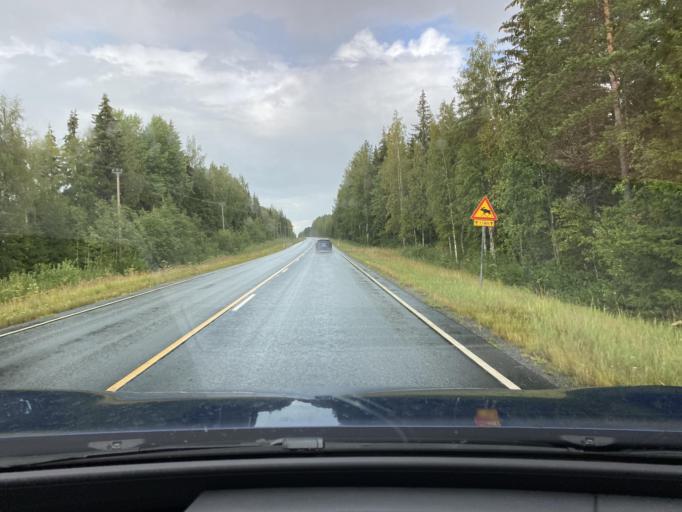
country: FI
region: Pirkanmaa
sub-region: Tampere
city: Haemeenkyroe
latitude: 61.5800
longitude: 23.1067
